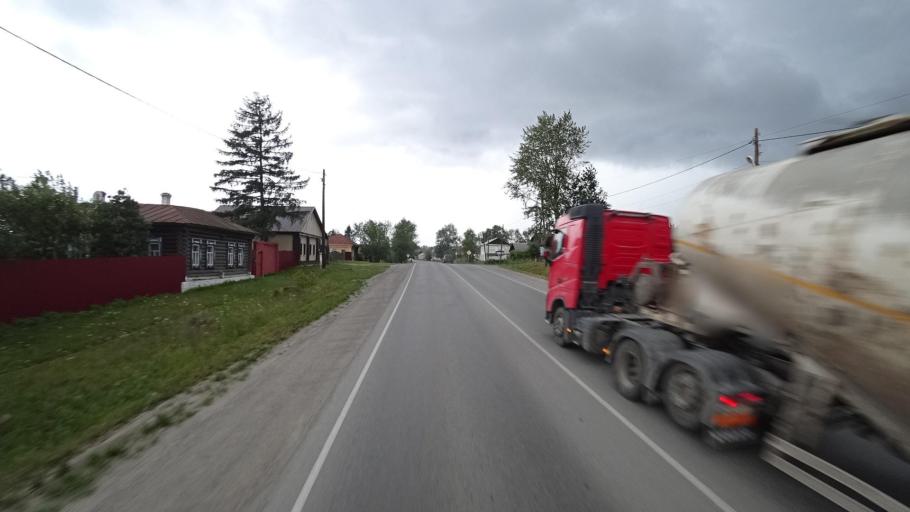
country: RU
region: Sverdlovsk
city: Kamyshlov
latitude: 56.8467
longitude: 62.6771
